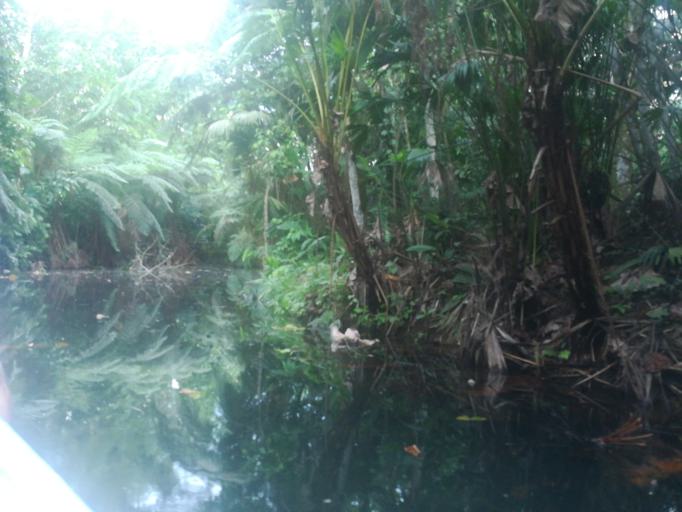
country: EC
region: Napo
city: Tena
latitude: -1.0417
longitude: -77.6649
